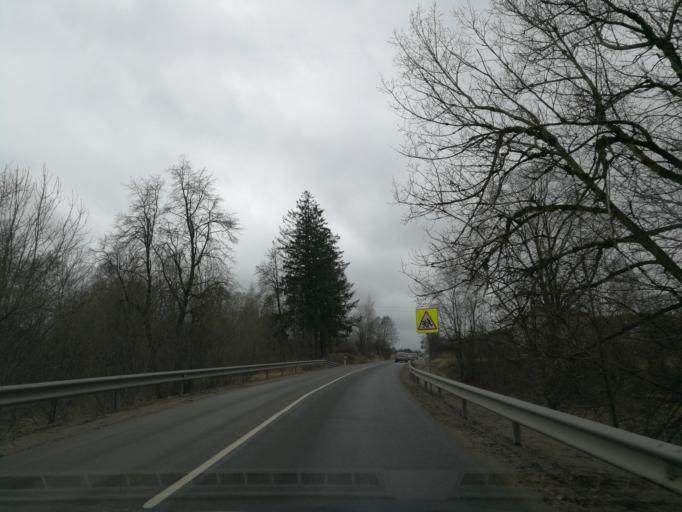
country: LT
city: Grigiskes
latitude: 54.6477
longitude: 25.1176
